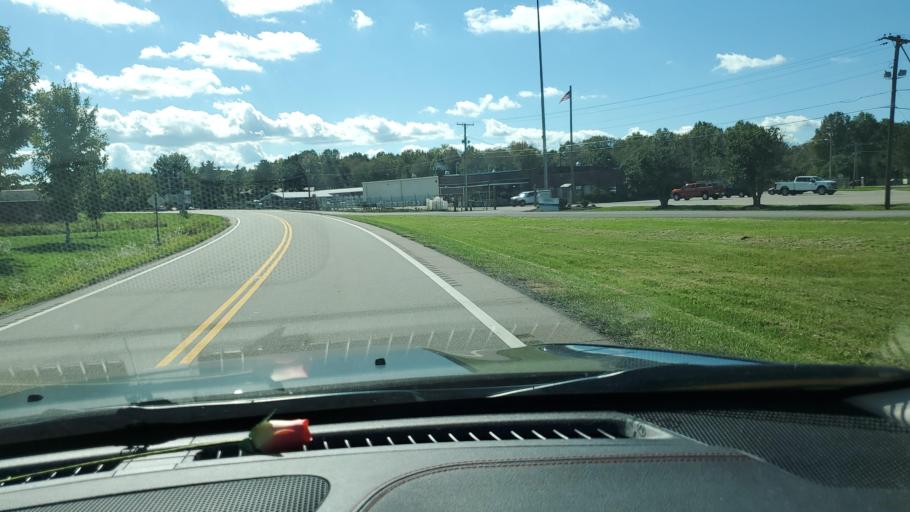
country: US
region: Ohio
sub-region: Trumbull County
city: Cortland
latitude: 41.4389
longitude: -80.5993
